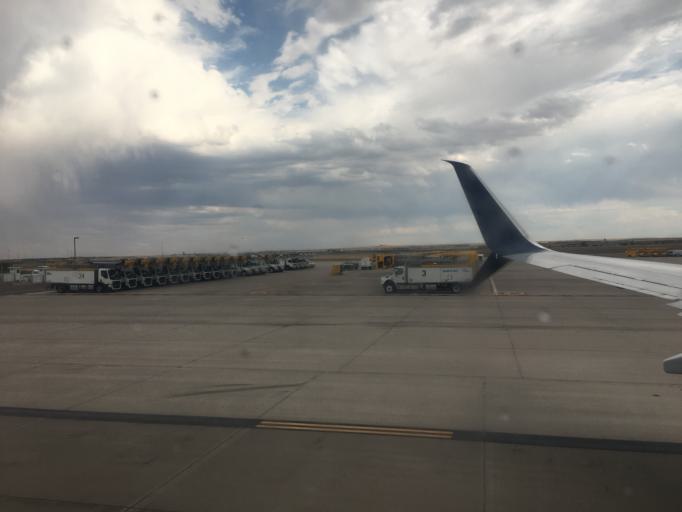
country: US
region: Colorado
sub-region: Weld County
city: Lochbuie
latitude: 39.8519
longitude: -104.6874
